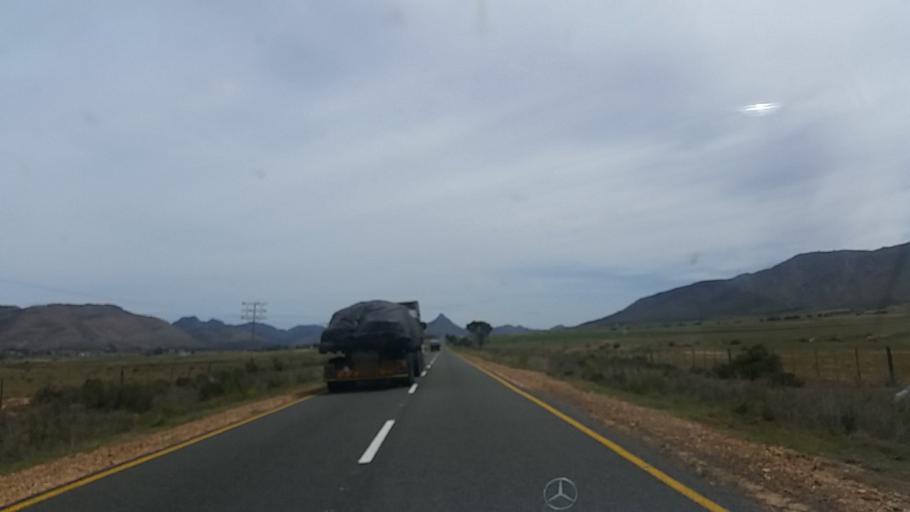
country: ZA
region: Western Cape
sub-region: Eden District Municipality
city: George
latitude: -33.8121
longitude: 22.5338
